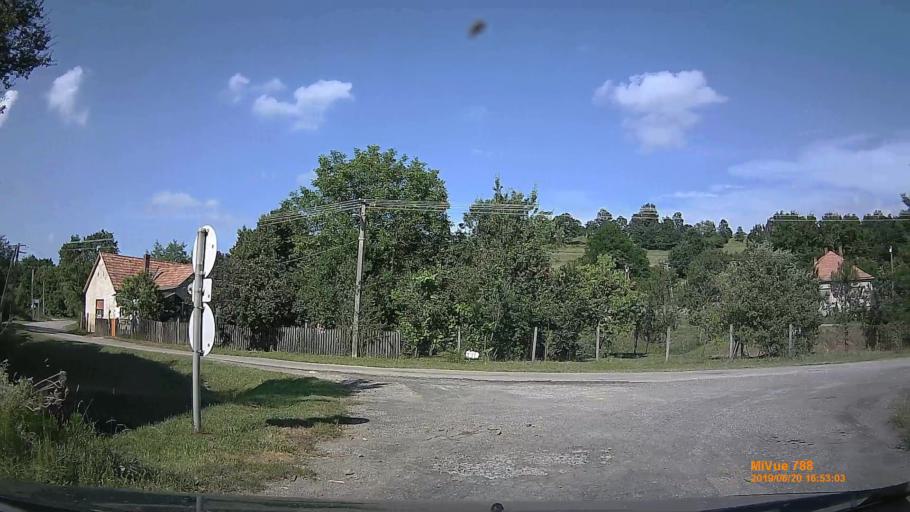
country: HU
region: Baranya
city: Buekkoesd
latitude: 46.1554
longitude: 18.0572
